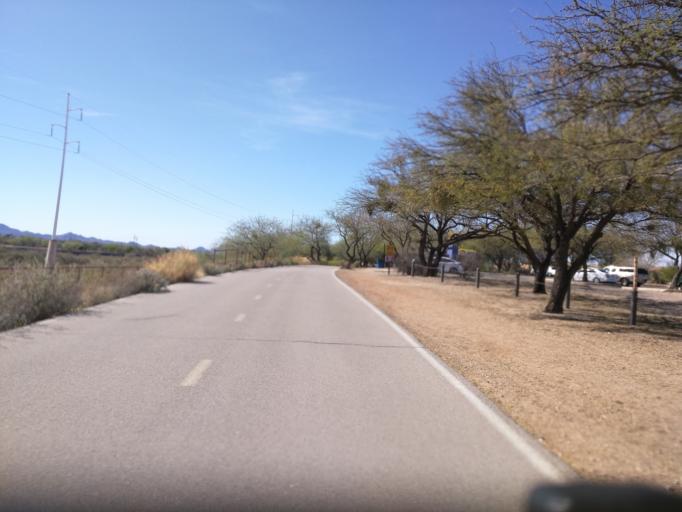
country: US
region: Arizona
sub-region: Pima County
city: Flowing Wells
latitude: 32.2964
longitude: -110.9989
